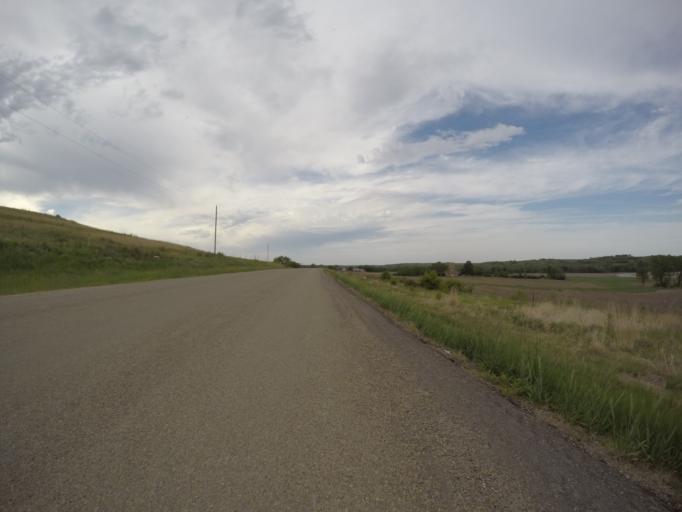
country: US
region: Kansas
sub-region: Riley County
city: Ogden
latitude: 39.0490
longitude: -96.6415
